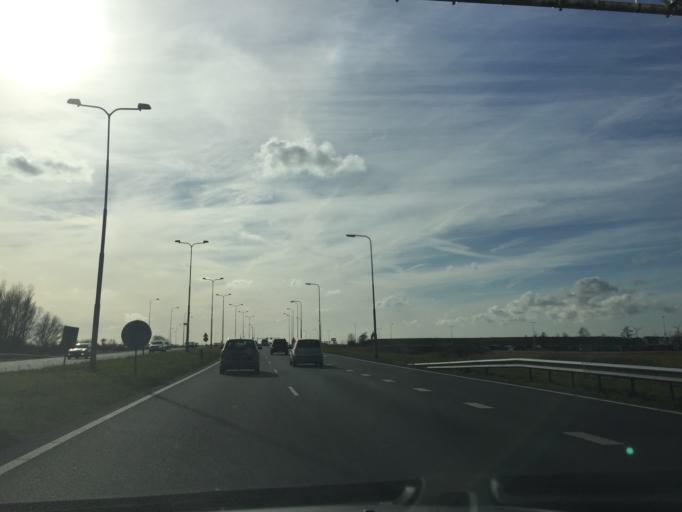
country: NL
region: South Holland
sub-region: Gemeente Alphen aan den Rijn
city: Alphen aan den Rijn
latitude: 52.1106
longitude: 4.6609
